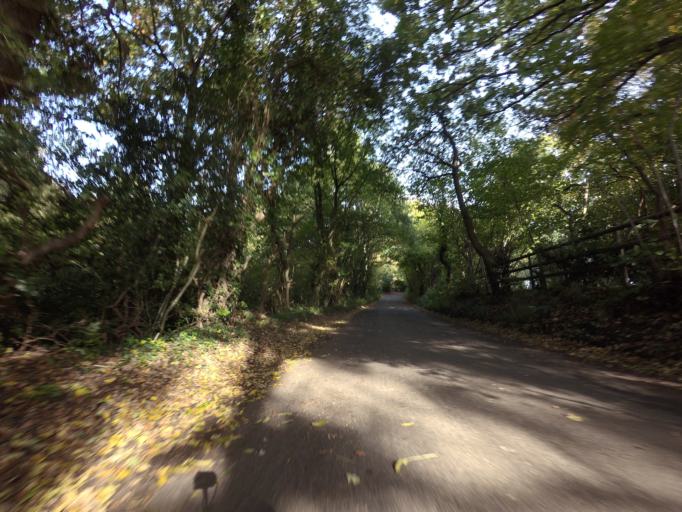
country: GB
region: England
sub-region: Kent
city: Swanley
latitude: 51.3874
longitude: 0.1598
